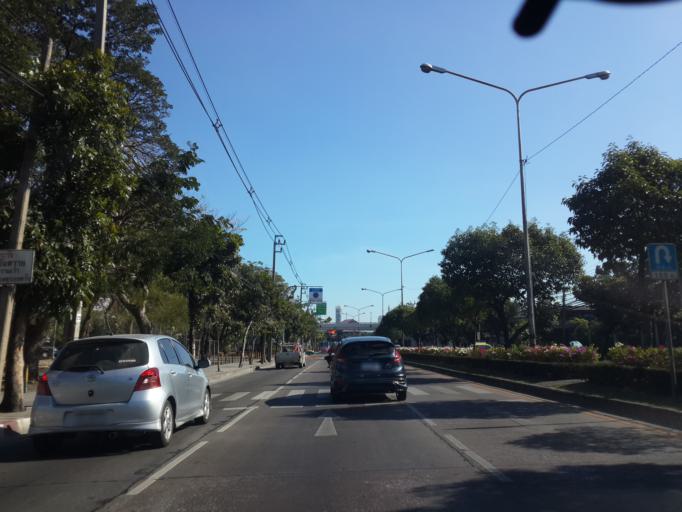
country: TH
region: Bangkok
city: Bang Kapi
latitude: 13.7772
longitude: 100.6448
